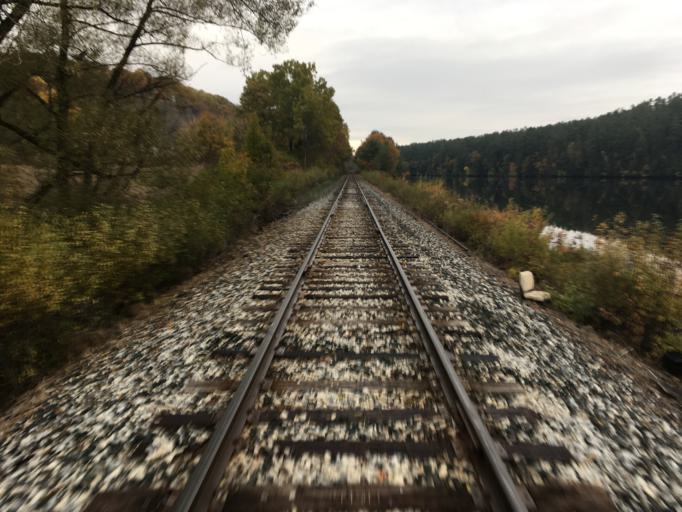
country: US
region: New Hampshire
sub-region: Grafton County
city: Hanover
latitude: 43.7141
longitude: -72.2908
